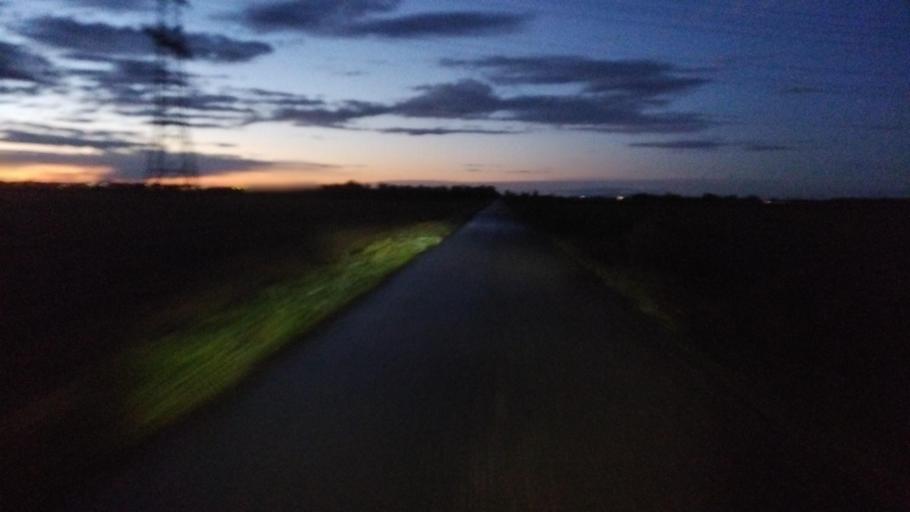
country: DE
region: Hesse
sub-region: Regierungsbezirk Darmstadt
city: Gross-Rohrheim
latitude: 49.7046
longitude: 8.5010
